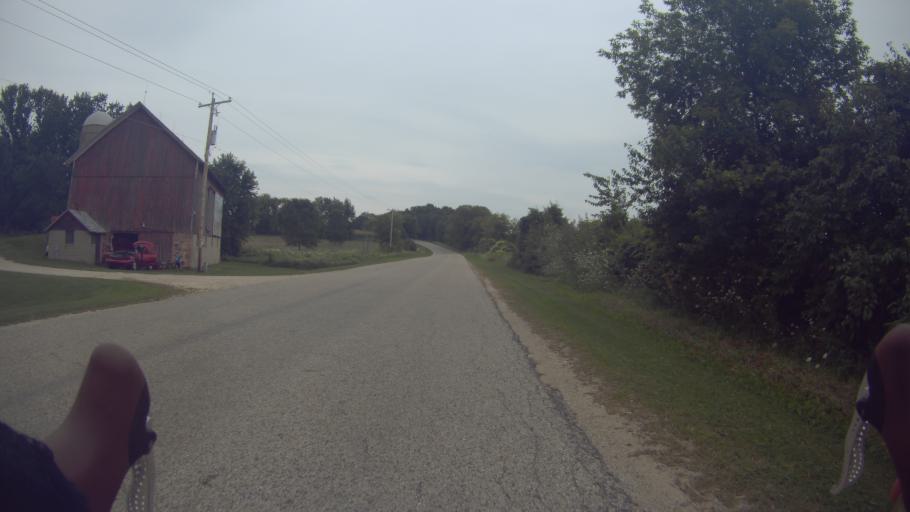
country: US
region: Wisconsin
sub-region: Jefferson County
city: Lake Mills
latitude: 43.1076
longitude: -88.9495
